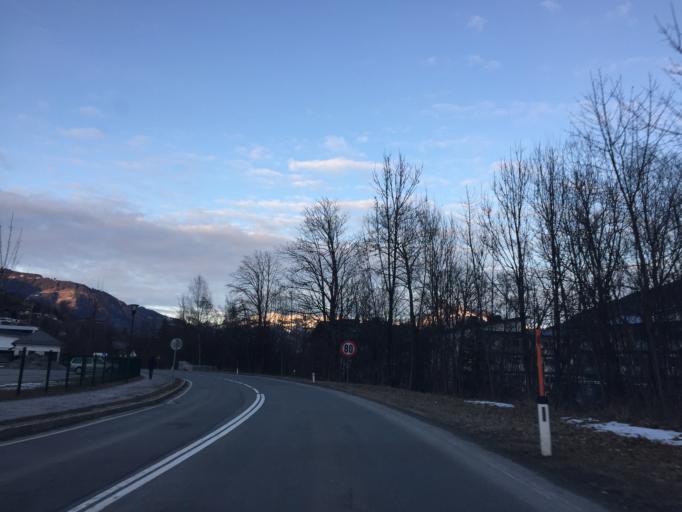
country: AT
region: Salzburg
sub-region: Politischer Bezirk Zell am See
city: Kaprun
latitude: 47.2615
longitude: 12.7443
